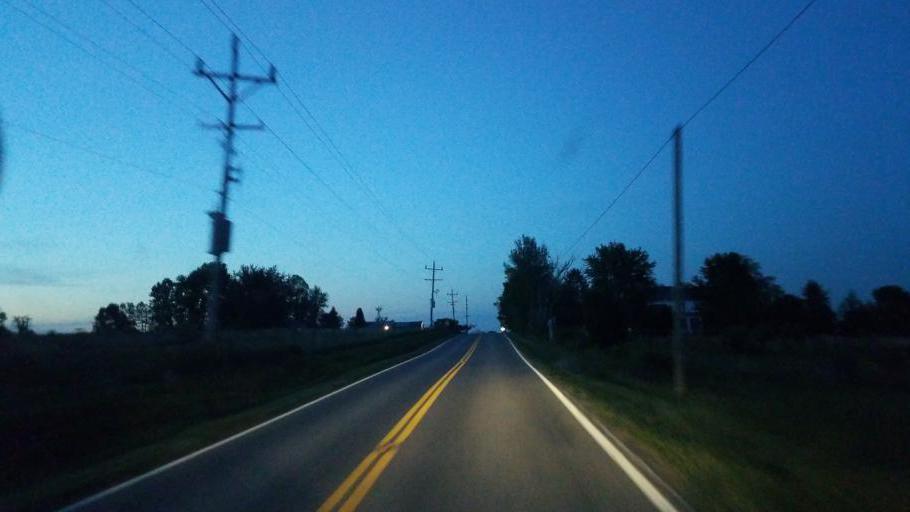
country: US
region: Ohio
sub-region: Highland County
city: Greenfield
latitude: 39.2882
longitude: -83.4125
